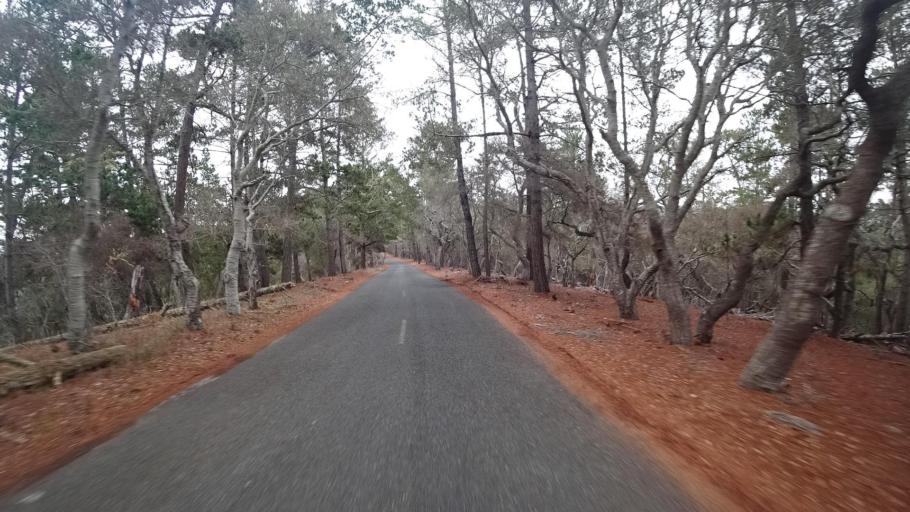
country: US
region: California
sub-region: Monterey County
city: Monterey
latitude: 36.5644
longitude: -121.8705
